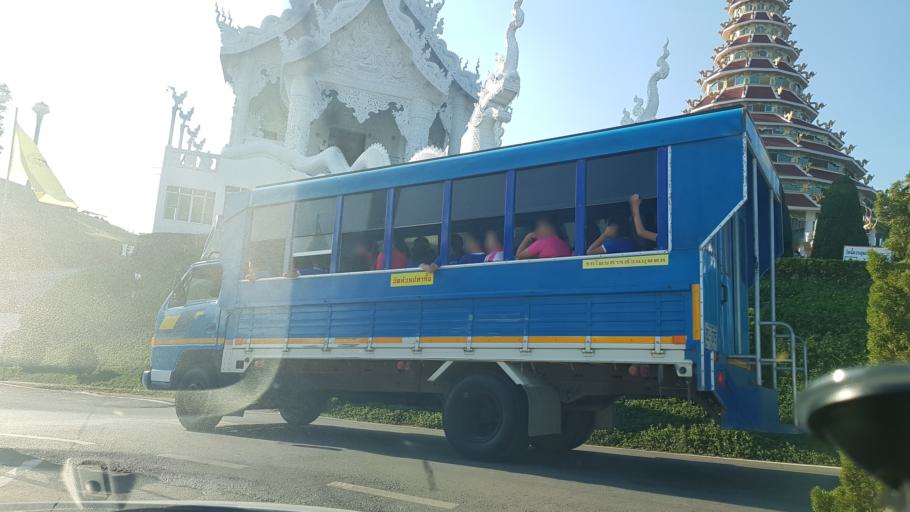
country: TH
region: Chiang Rai
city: Chiang Rai
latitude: 19.9492
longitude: 99.8071
